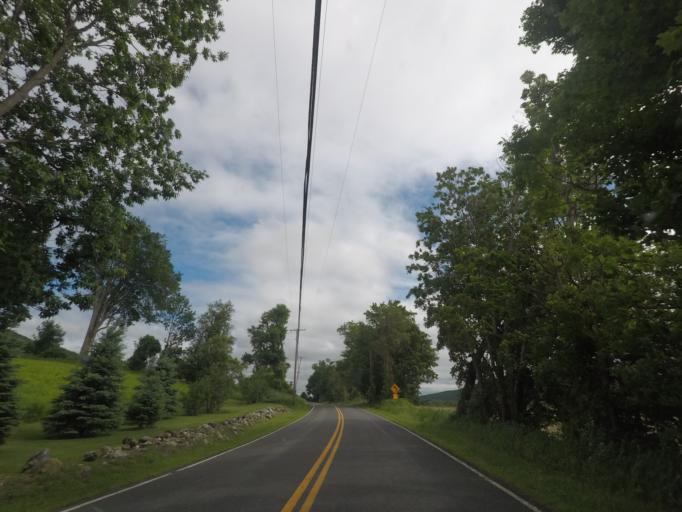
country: US
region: New York
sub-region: Dutchess County
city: Pine Plains
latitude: 42.0280
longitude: -73.5160
